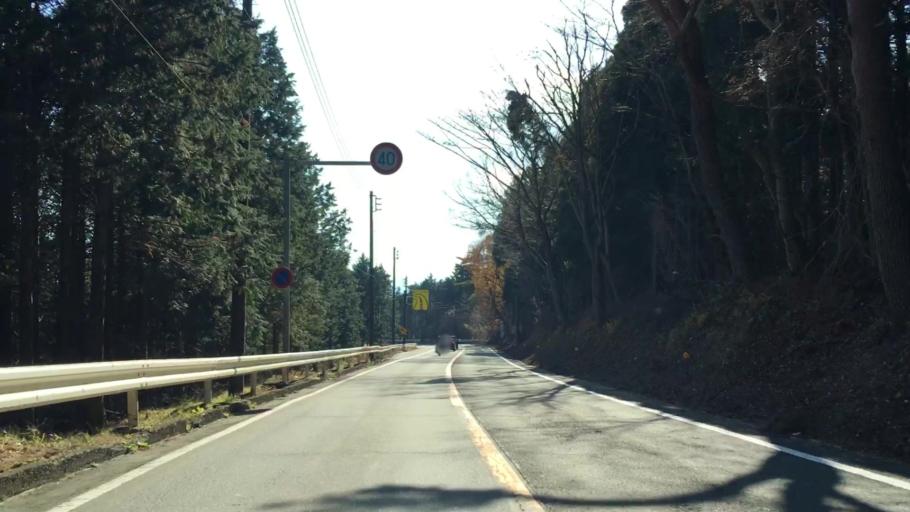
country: JP
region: Shizuoka
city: Gotemba
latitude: 35.3818
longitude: 138.8500
